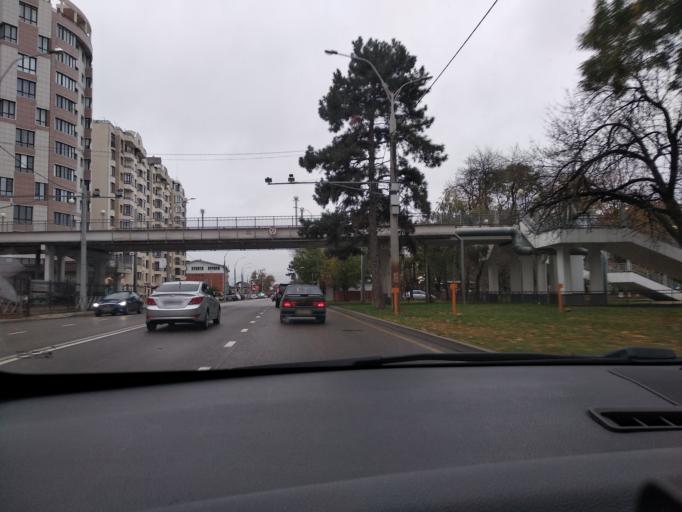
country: RU
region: Adygeya
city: Yablonovskiy
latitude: 45.0167
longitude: 38.9586
